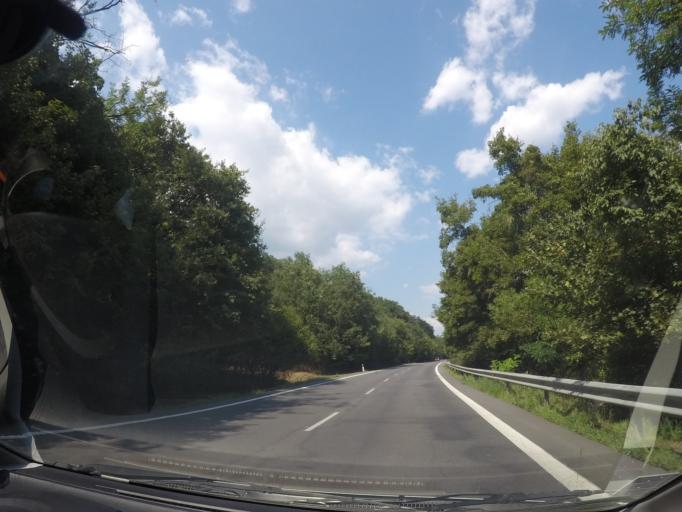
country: SK
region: Banskobystricky
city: Dudince
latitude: 48.2499
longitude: 18.9704
